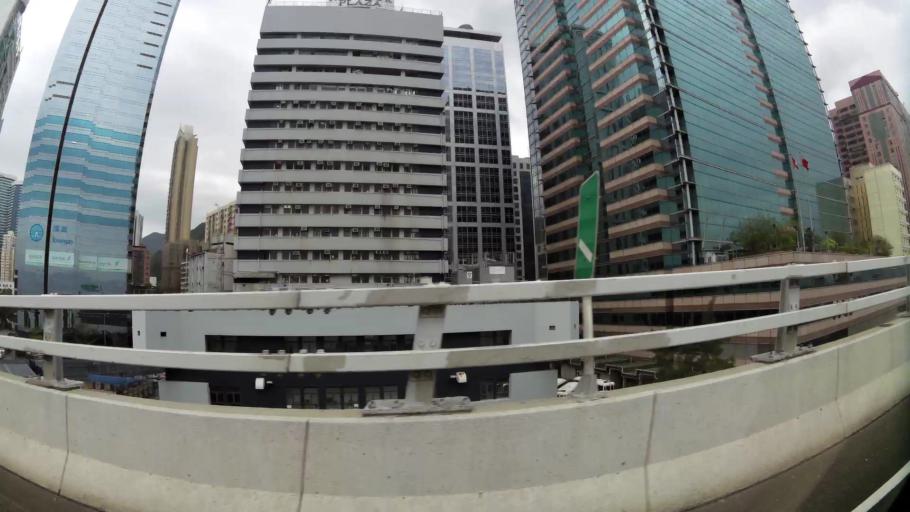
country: HK
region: Kowloon City
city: Kowloon
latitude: 22.2926
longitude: 114.2092
